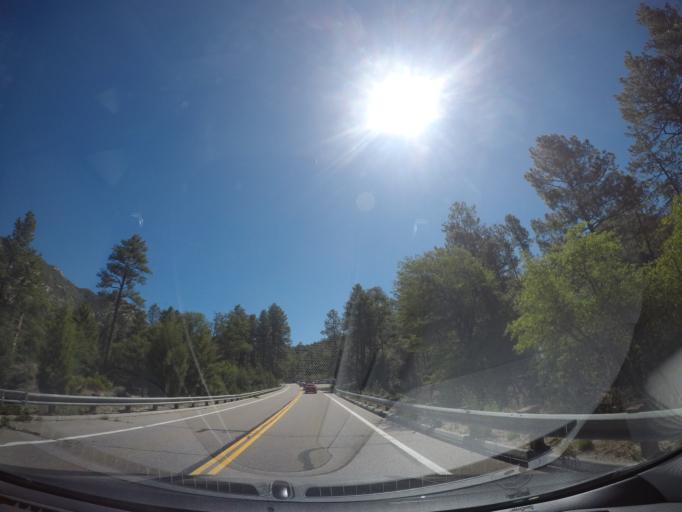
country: US
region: Arizona
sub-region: Pima County
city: Tanque Verde
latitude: 32.3739
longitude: -110.6916
